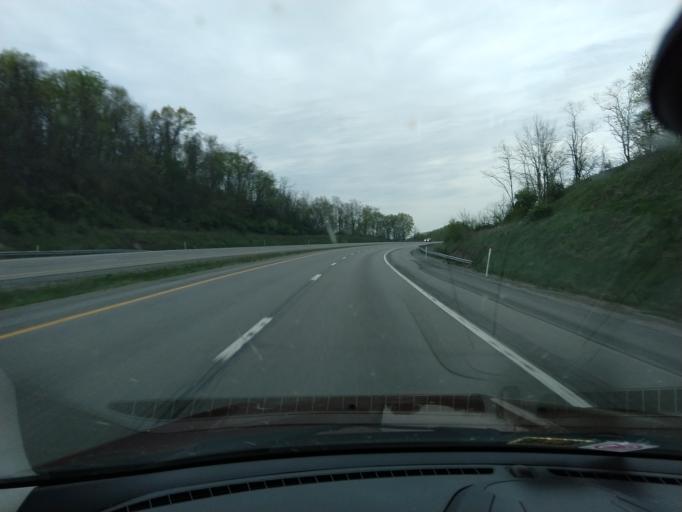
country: US
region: West Virginia
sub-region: Lewis County
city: Weston
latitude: 38.9332
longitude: -80.5437
